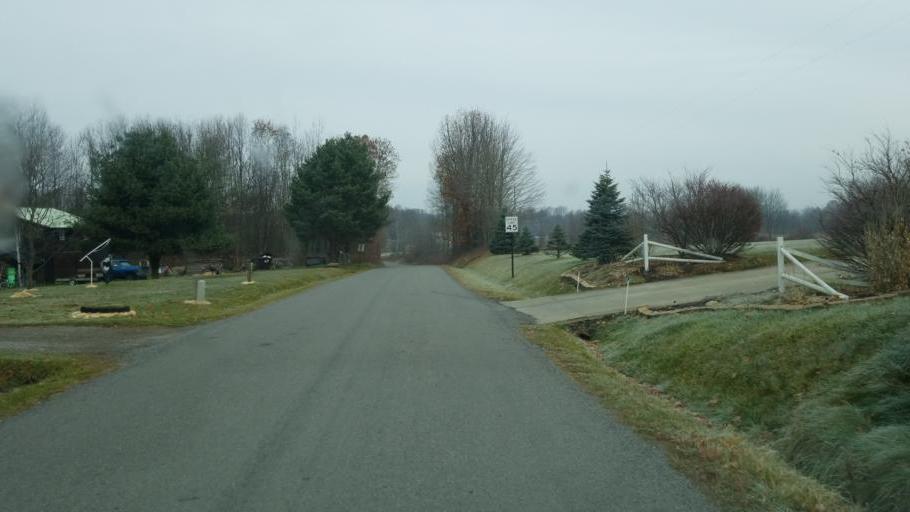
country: US
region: Pennsylvania
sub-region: Crawford County
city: Cochranton
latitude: 41.5152
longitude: -80.1209
